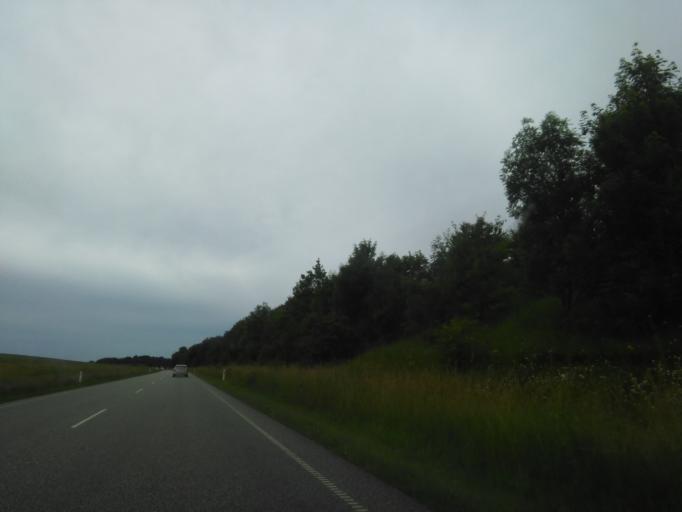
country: DK
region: Central Jutland
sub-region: Horsens Kommune
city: Horsens
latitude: 55.9122
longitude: 9.9072
